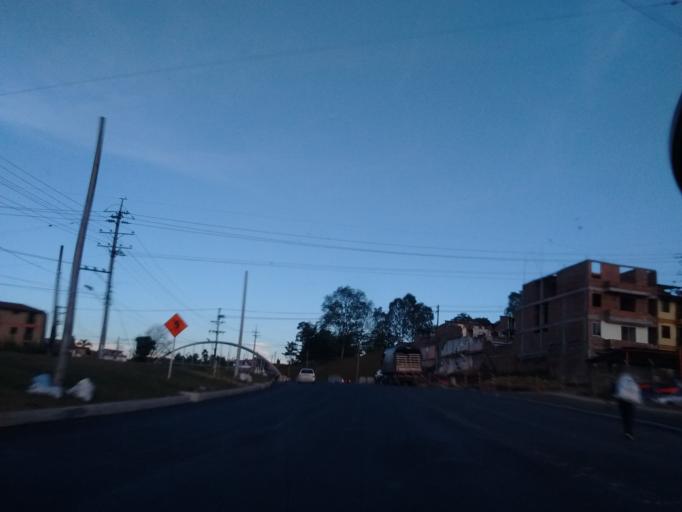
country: CO
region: Antioquia
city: Marinilla
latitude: 6.1686
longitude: -75.3388
